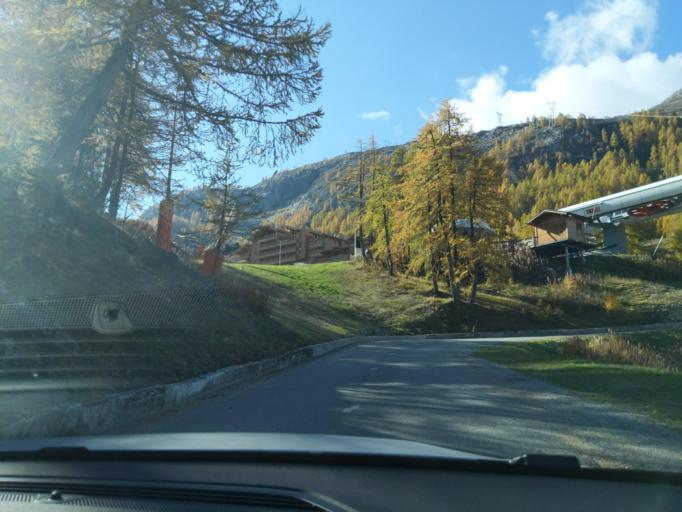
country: FR
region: Rhone-Alpes
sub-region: Departement de la Savoie
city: Tignes
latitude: 45.4988
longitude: 6.9241
